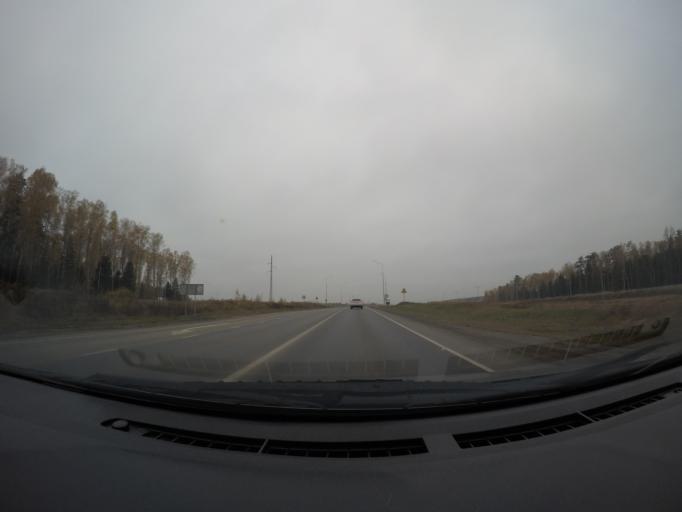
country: RU
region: Moskovskaya
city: Vostryakovo
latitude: 55.3345
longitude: 37.7688
